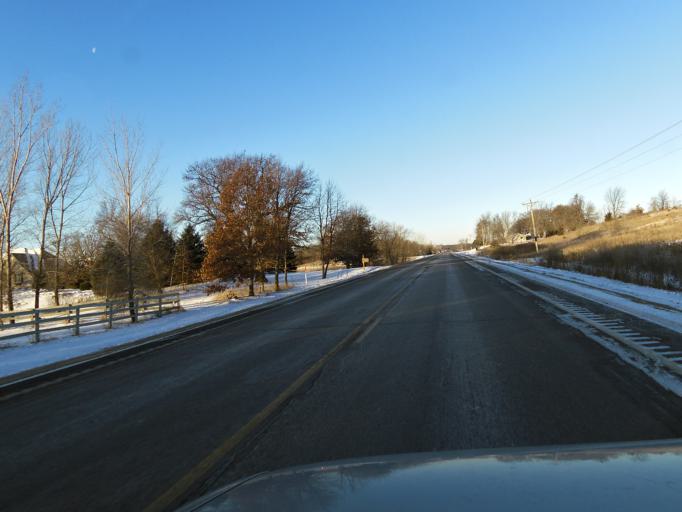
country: US
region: Minnesota
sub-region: Scott County
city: Prior Lake
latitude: 44.6743
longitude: -93.4020
